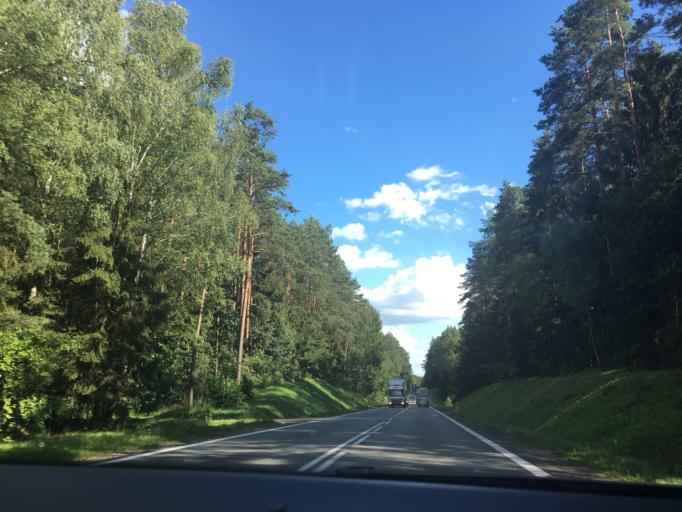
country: PL
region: Podlasie
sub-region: Powiat bialostocki
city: Wasilkow
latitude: 53.2616
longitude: 23.1353
